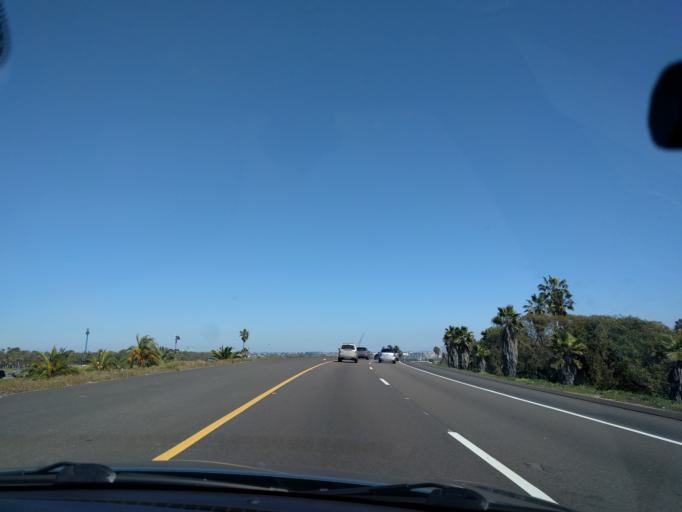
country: US
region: California
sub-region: San Diego County
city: Coronado
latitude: 32.7551
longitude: -117.2350
